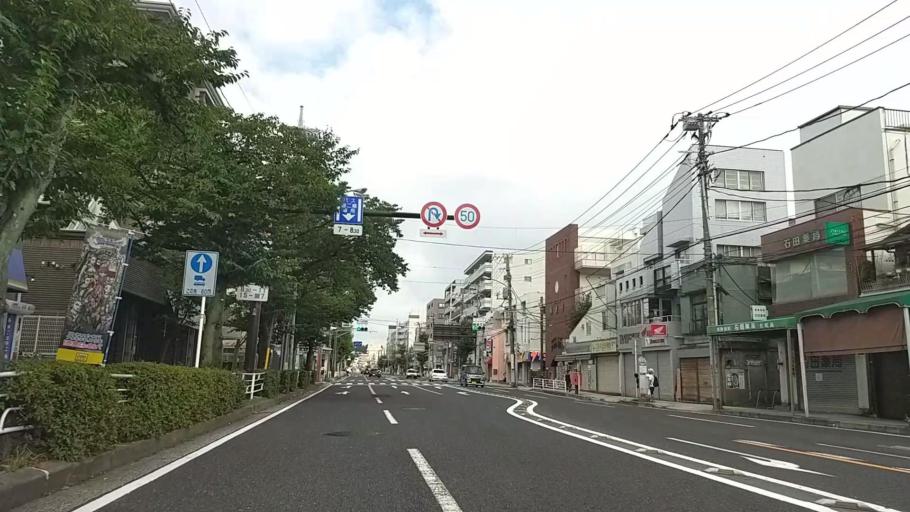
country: JP
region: Kanagawa
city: Yokohama
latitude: 35.4293
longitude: 139.6634
